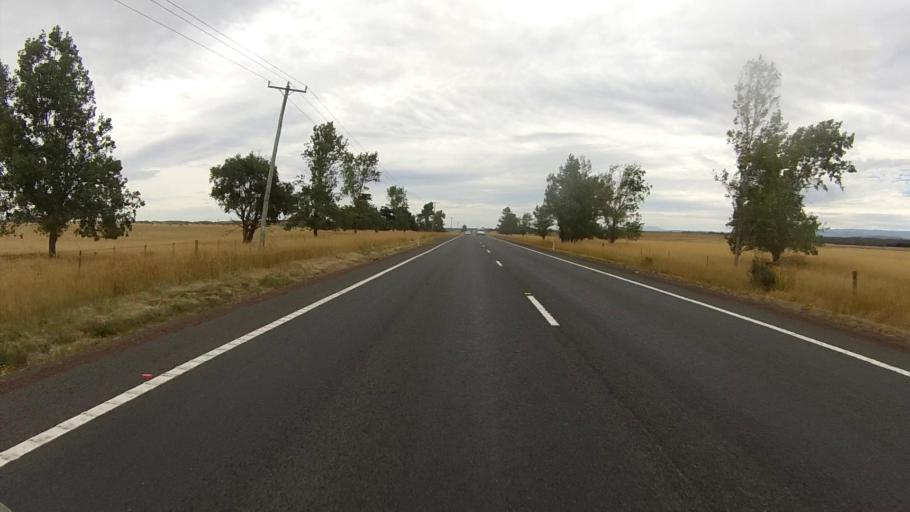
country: AU
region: Tasmania
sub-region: Northern Midlands
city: Evandale
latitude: -41.8906
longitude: 147.4704
